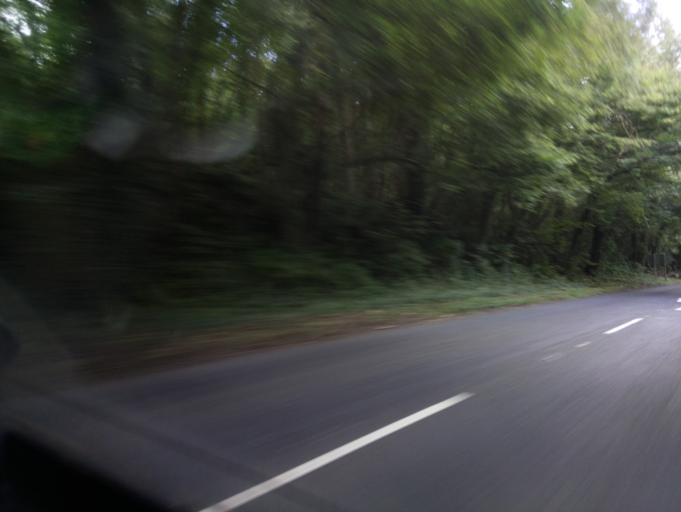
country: GB
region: England
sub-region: Wiltshire
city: Box
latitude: 51.4081
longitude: -2.2408
